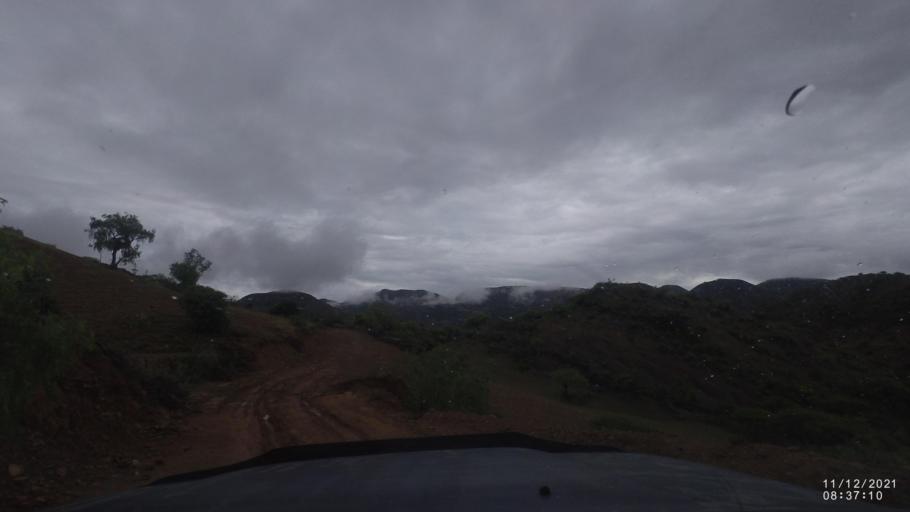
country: BO
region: Cochabamba
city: Tarata
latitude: -17.9269
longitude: -65.9370
